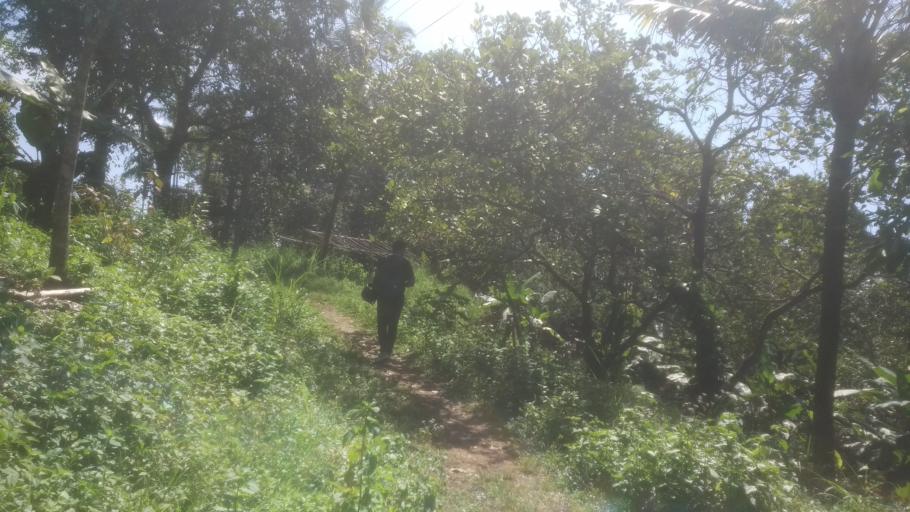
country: IN
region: Kerala
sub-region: Idukki
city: Idukki
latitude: 9.9763
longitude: 76.8362
